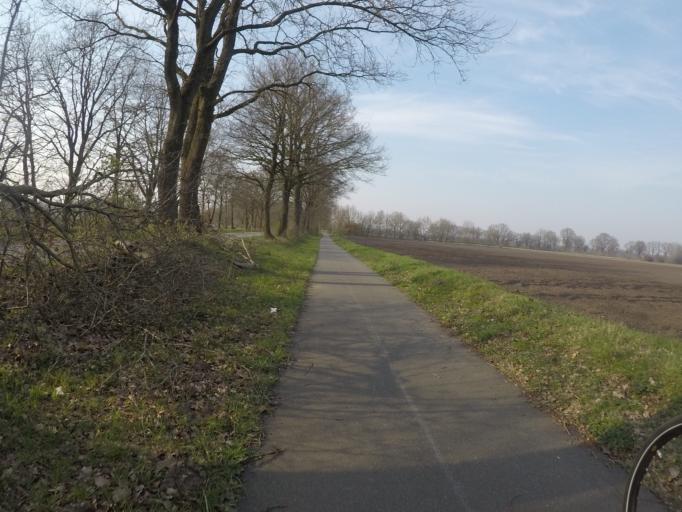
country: DE
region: Schleswig-Holstein
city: Wahlstedt
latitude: 53.9656
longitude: 10.1916
